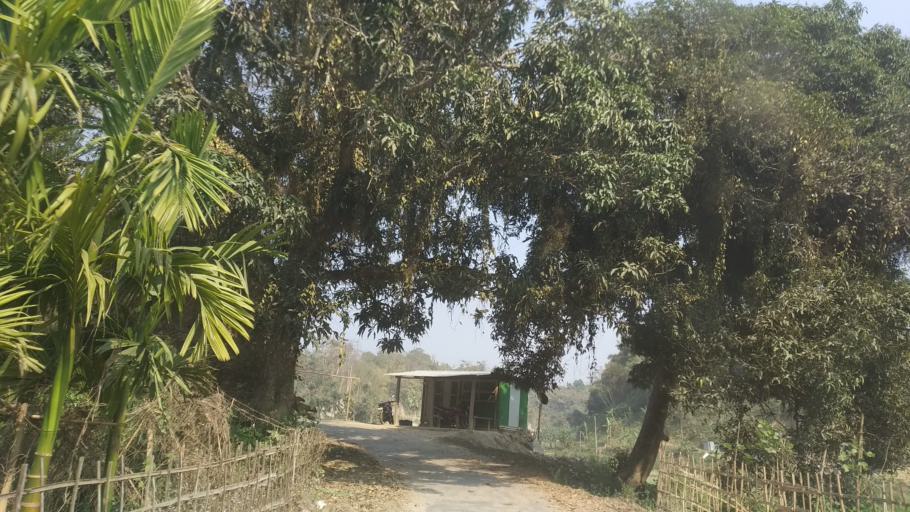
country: IN
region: Tripura
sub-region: West Tripura
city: Sonamura
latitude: 23.5231
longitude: 91.2586
